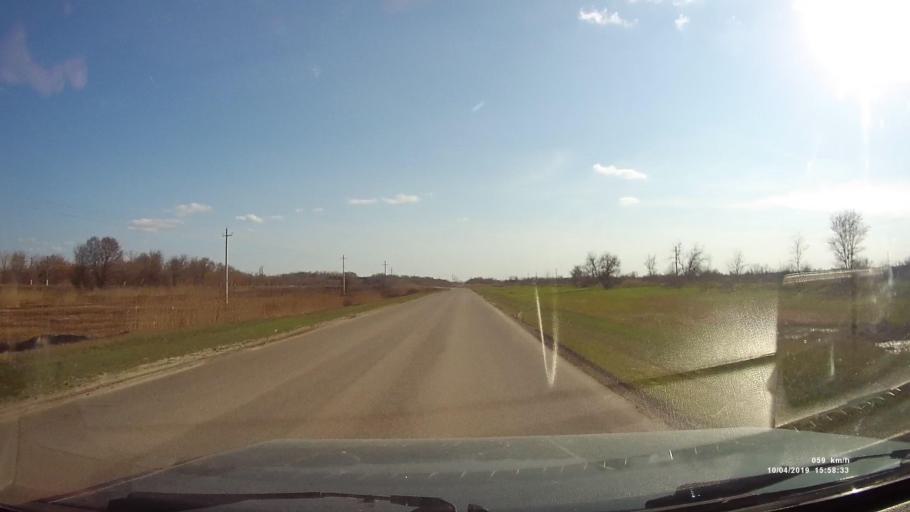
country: RU
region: Rostov
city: Masalovka
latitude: 48.4022
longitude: 40.2718
